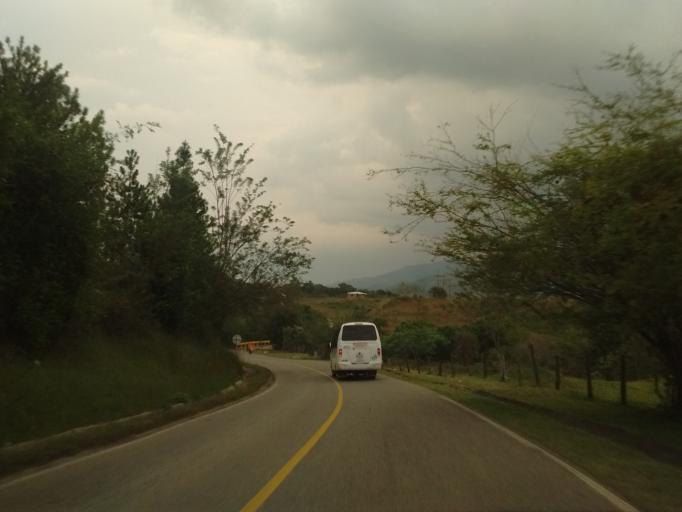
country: CO
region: Cauca
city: Caloto
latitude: 3.0584
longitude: -76.3725
